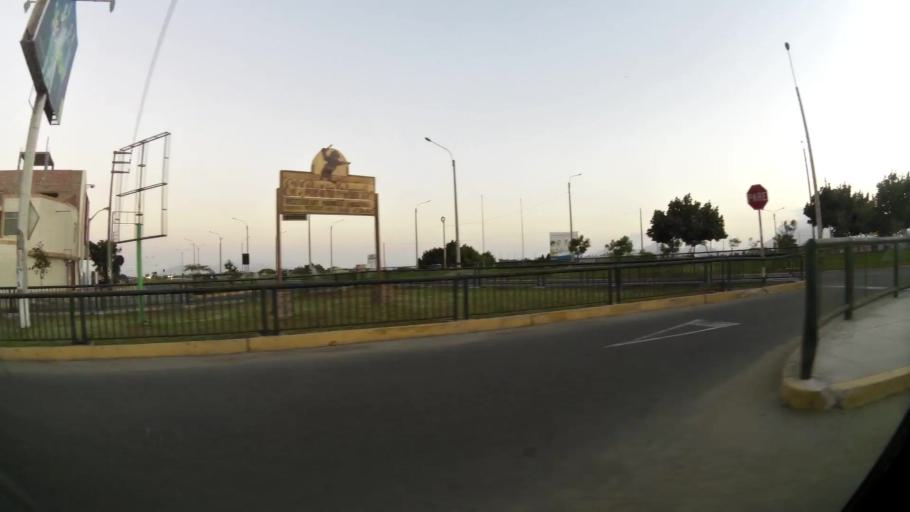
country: PE
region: Ancash
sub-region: Provincia de Santa
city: Buenos Aires
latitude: -9.1261
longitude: -78.5335
